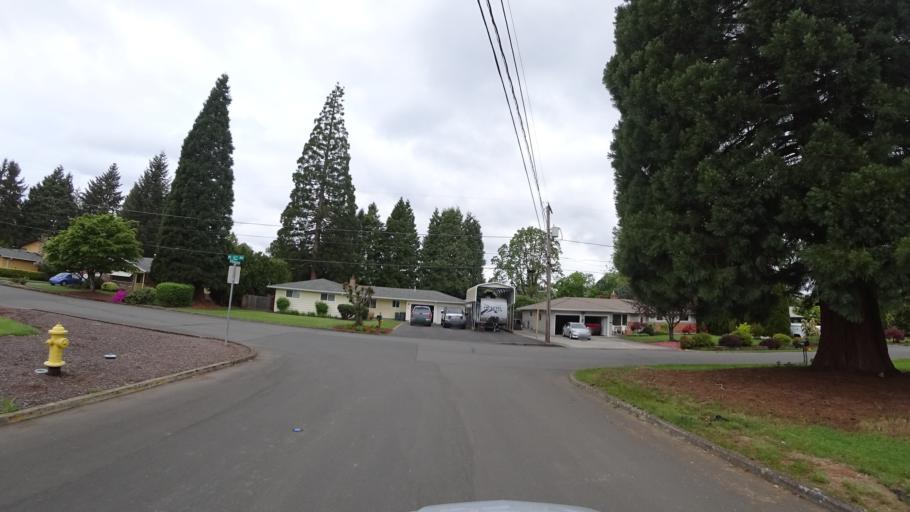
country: US
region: Oregon
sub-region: Washington County
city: Hillsboro
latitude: 45.5294
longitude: -122.9802
